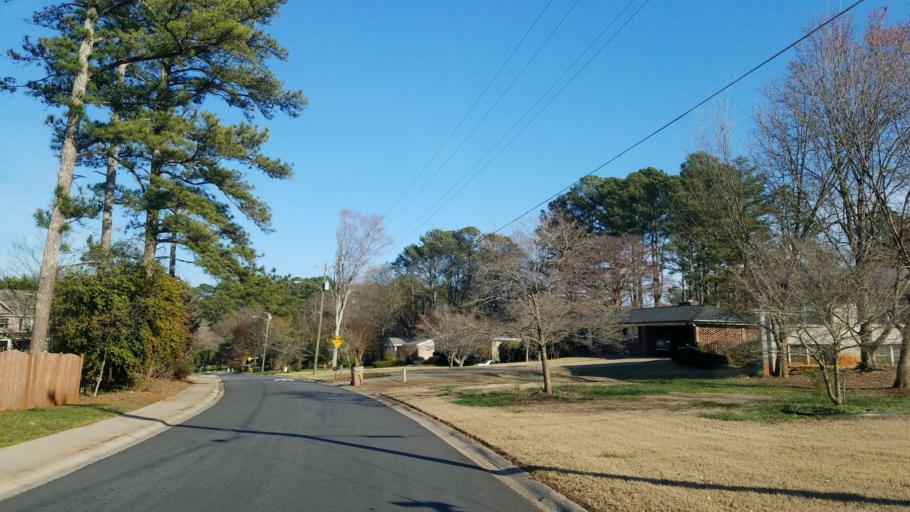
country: US
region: Georgia
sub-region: Cobb County
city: Marietta
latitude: 33.9999
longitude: -84.5027
